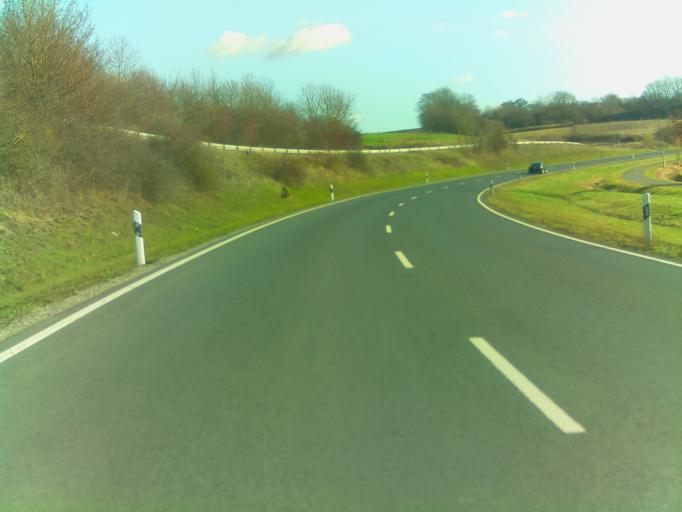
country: DE
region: Bavaria
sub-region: Regierungsbezirk Unterfranken
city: Grosseibstadt
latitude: 50.3017
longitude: 10.4244
